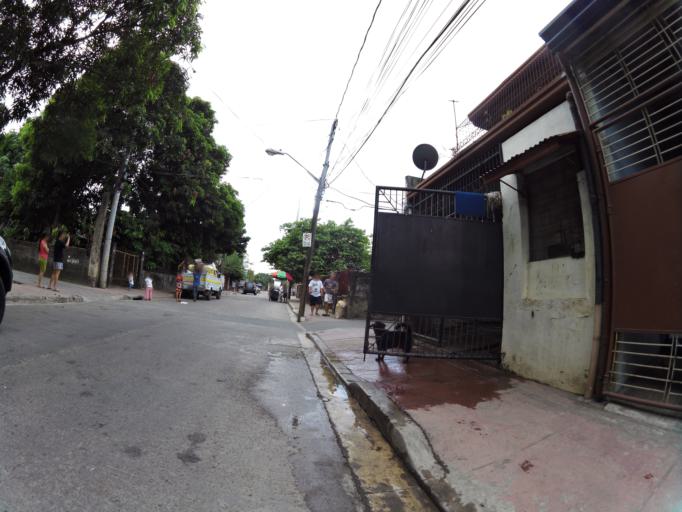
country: PH
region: Calabarzon
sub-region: Province of Rizal
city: Antipolo
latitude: 14.6405
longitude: 121.1112
